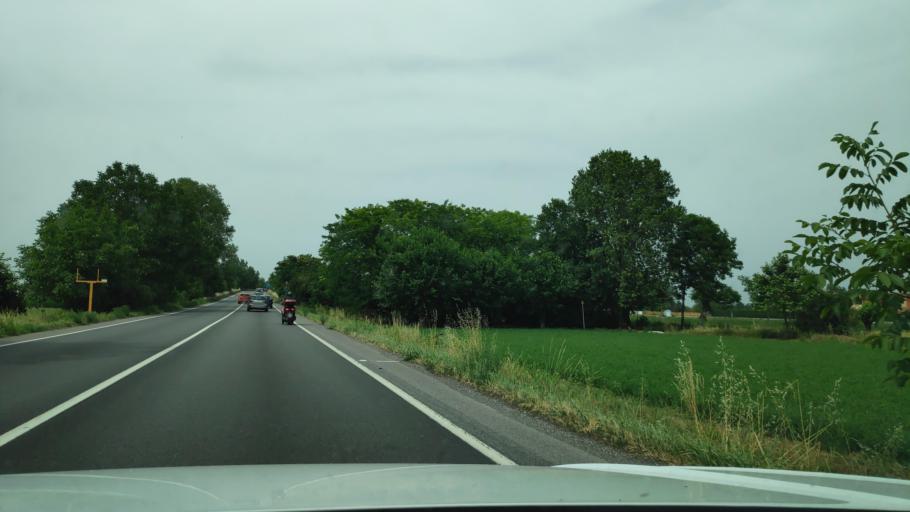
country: IT
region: Lombardy
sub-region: Provincia di Cremona
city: Soncino
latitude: 45.4027
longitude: 9.8568
